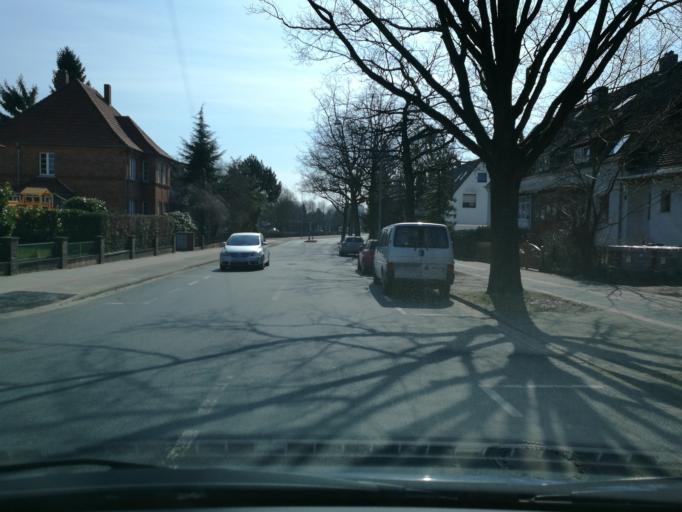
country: DE
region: Lower Saxony
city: Ronnenberg
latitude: 52.3711
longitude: 9.6691
